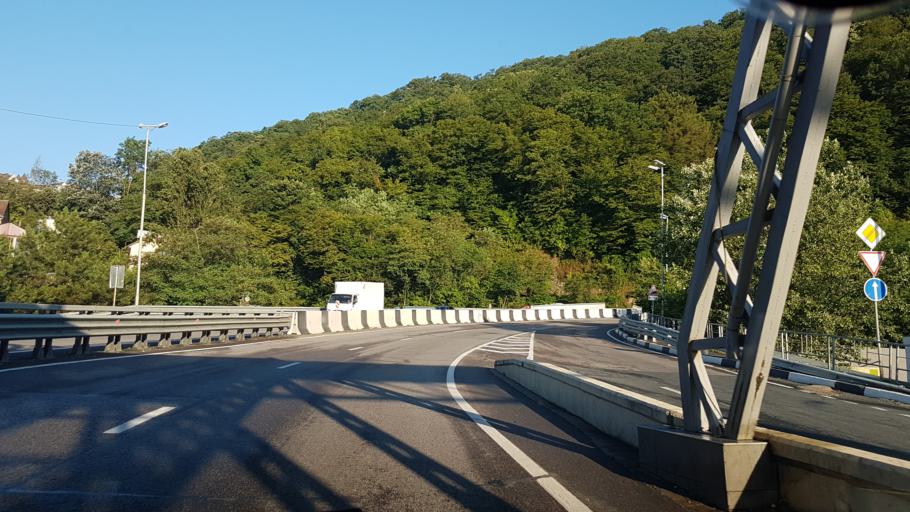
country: RU
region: Krasnodarskiy
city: Dagomys
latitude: 43.6394
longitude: 39.6991
